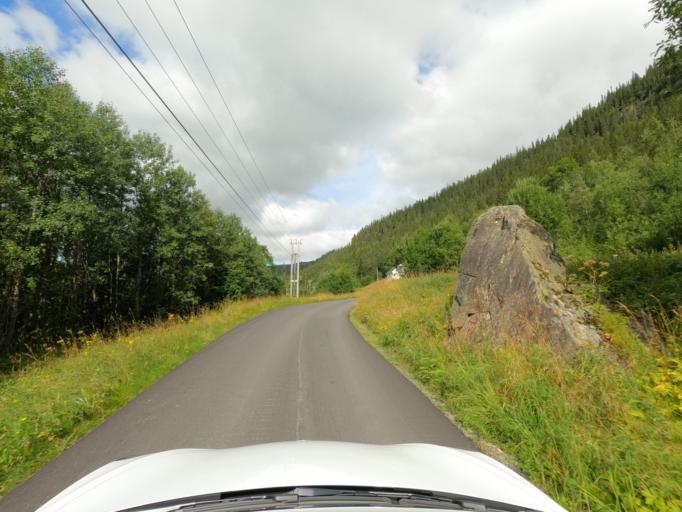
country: NO
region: Telemark
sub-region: Tinn
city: Rjukan
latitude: 60.0723
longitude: 8.7068
